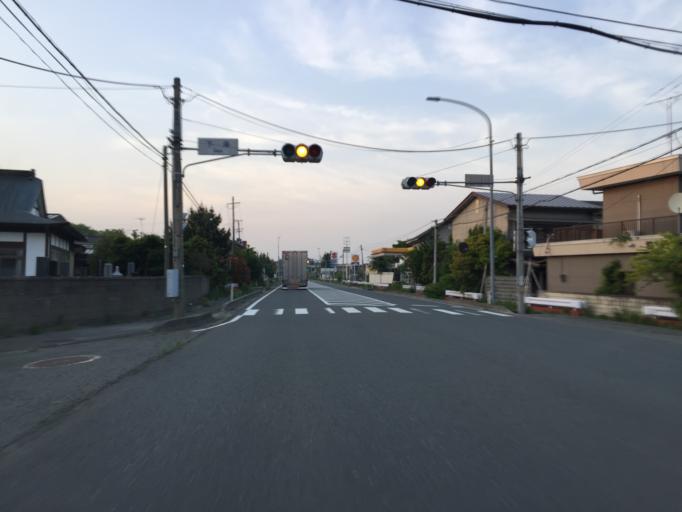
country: JP
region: Fukushima
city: Namie
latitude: 37.4481
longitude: 141.0087
